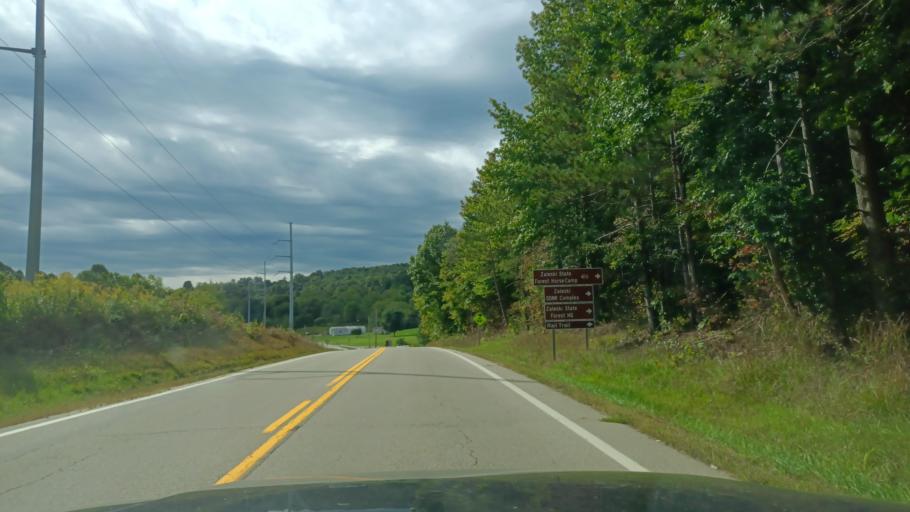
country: US
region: Ohio
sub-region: Vinton County
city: McArthur
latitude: 39.2409
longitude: -82.3640
